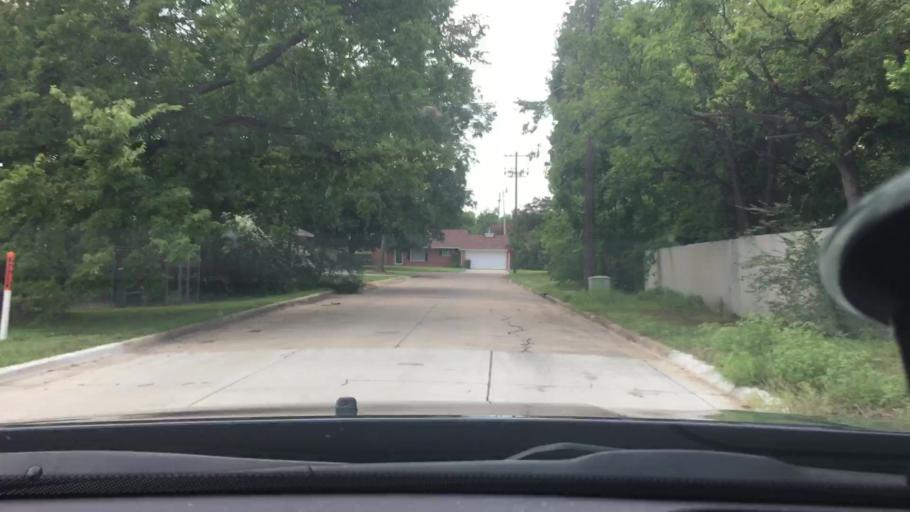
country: US
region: Oklahoma
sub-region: Carter County
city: Ardmore
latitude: 34.1707
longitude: -97.1446
